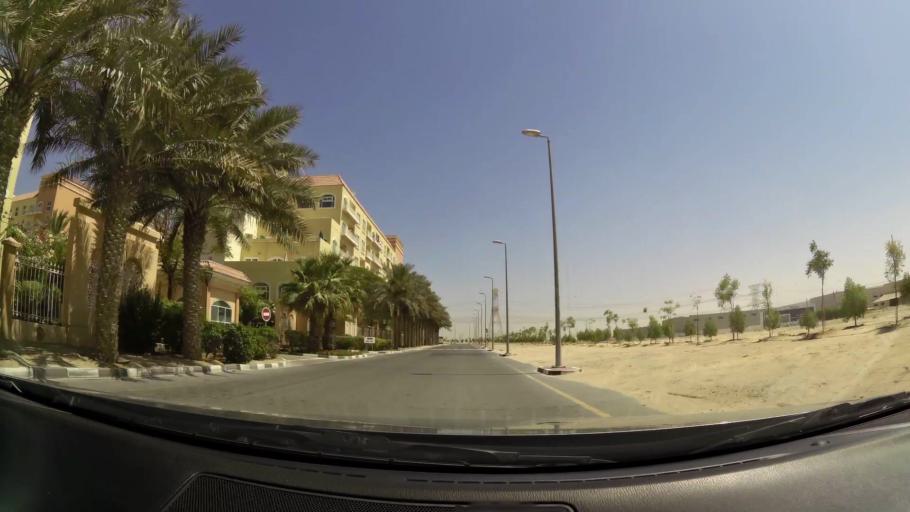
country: AE
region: Dubai
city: Dubai
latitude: 24.9878
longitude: 55.2041
